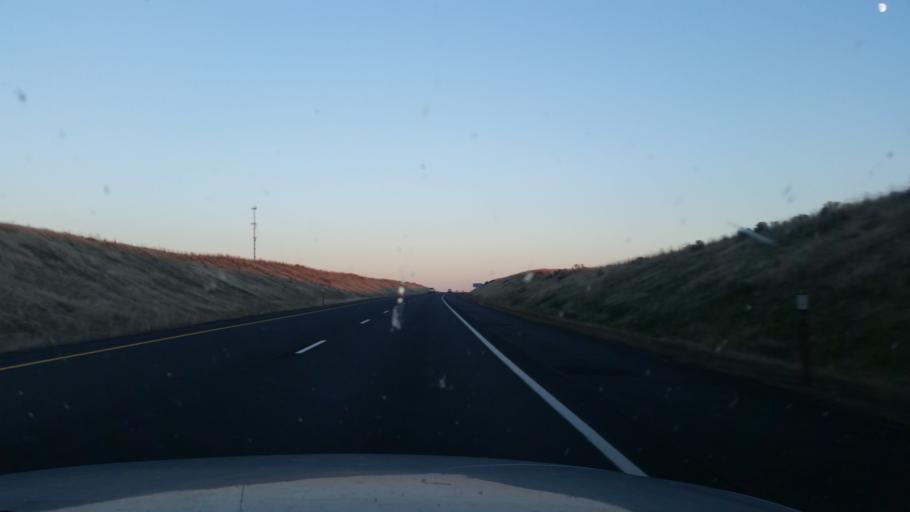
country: US
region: Washington
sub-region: Grant County
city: Warden
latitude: 47.0868
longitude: -118.8619
